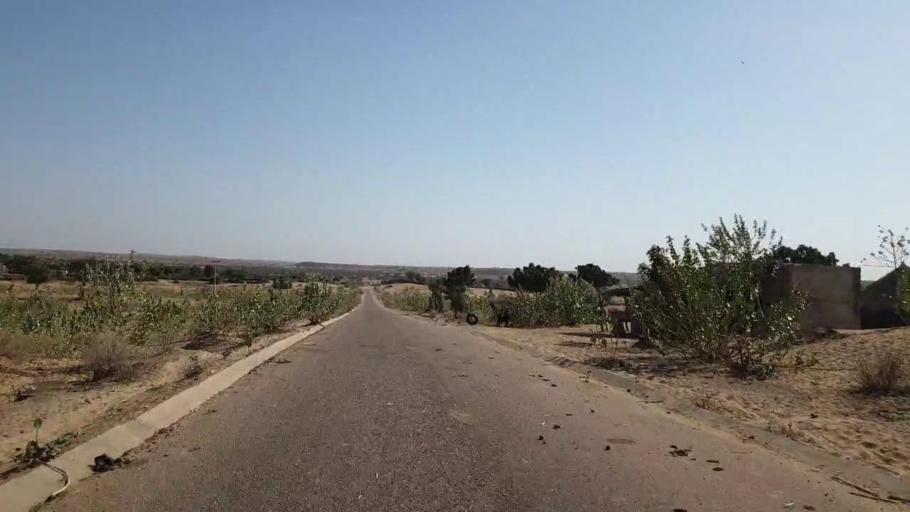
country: PK
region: Sindh
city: Umarkot
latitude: 25.1033
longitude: 70.0383
